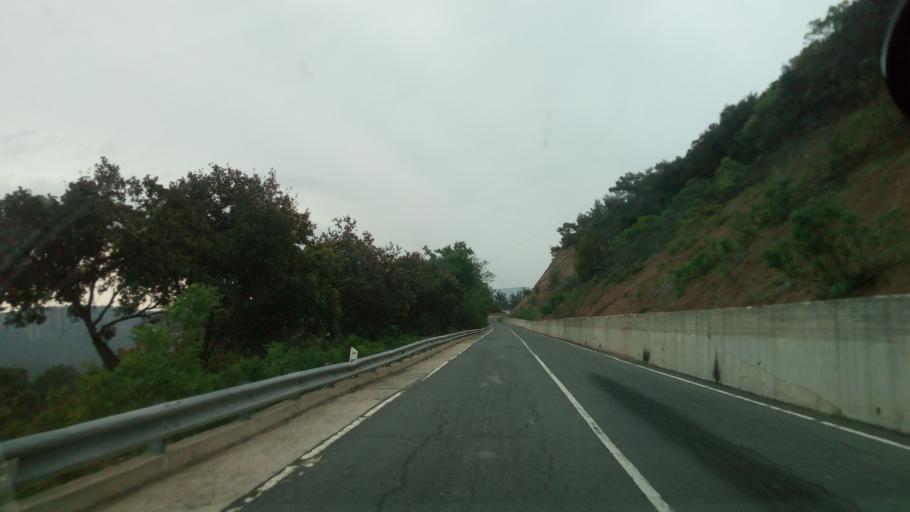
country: CY
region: Lefkosia
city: Kakopetria
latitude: 34.9874
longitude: 32.7407
